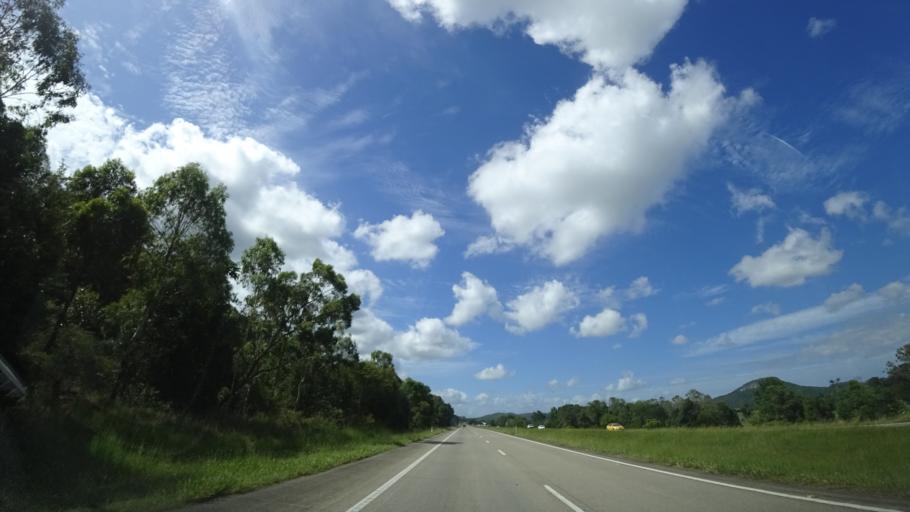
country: AU
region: Queensland
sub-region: Sunshine Coast
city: Yandina
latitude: -26.5768
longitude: 152.9629
